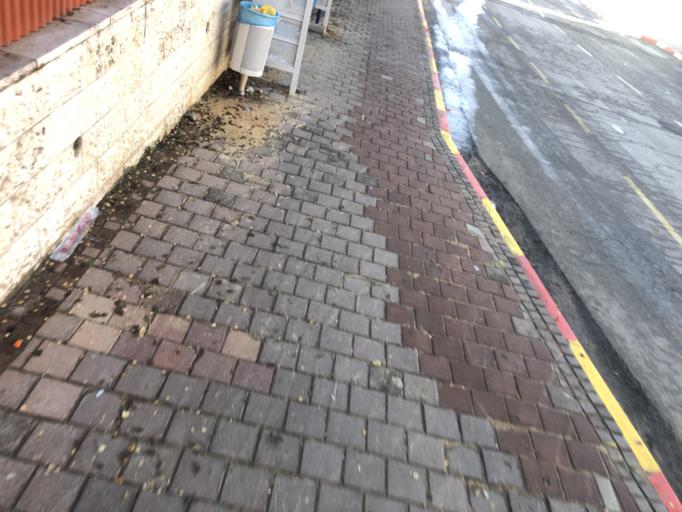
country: IL
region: Jerusalem
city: Modiin Ilit
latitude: 31.9230
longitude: 35.0516
